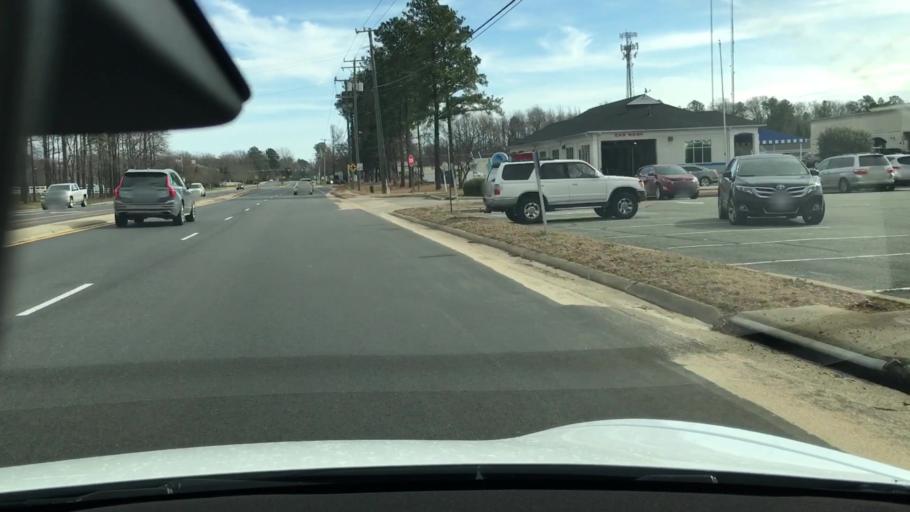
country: US
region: Virginia
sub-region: Chesterfield County
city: Bon Air
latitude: 37.5219
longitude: -77.6112
